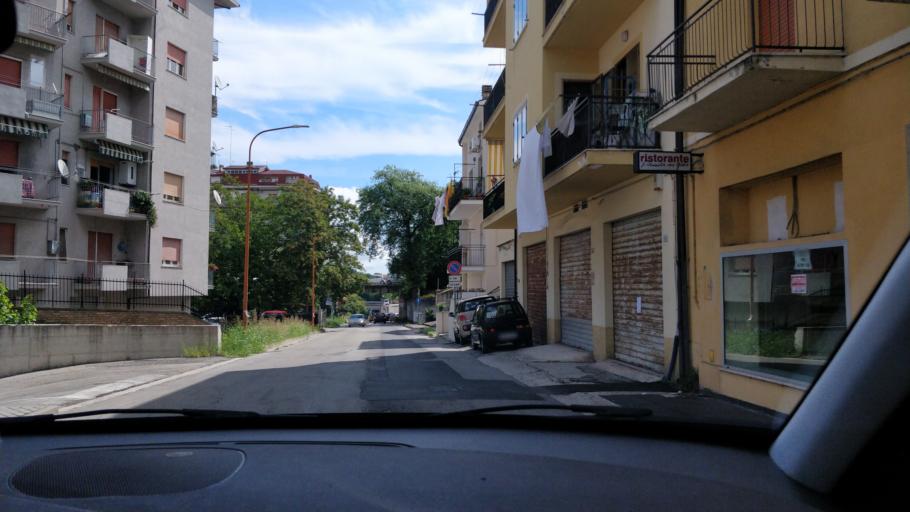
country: IT
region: Abruzzo
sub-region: Provincia di Chieti
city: Lanciano
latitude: 42.2290
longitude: 14.3981
